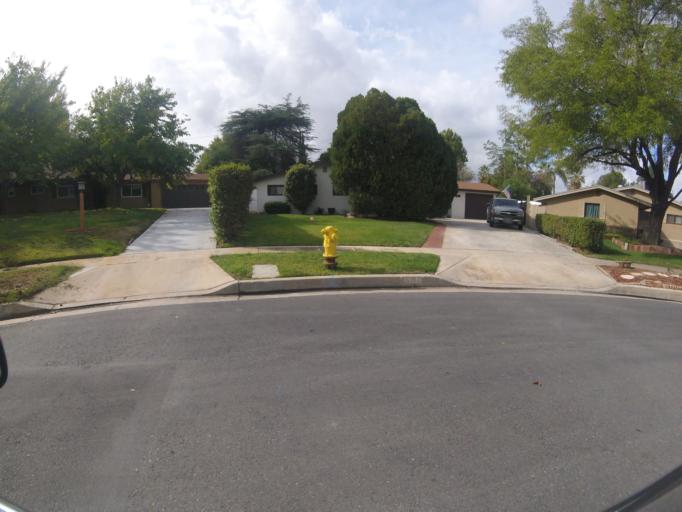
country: US
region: California
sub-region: San Bernardino County
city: Redlands
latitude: 34.0447
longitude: -117.1836
